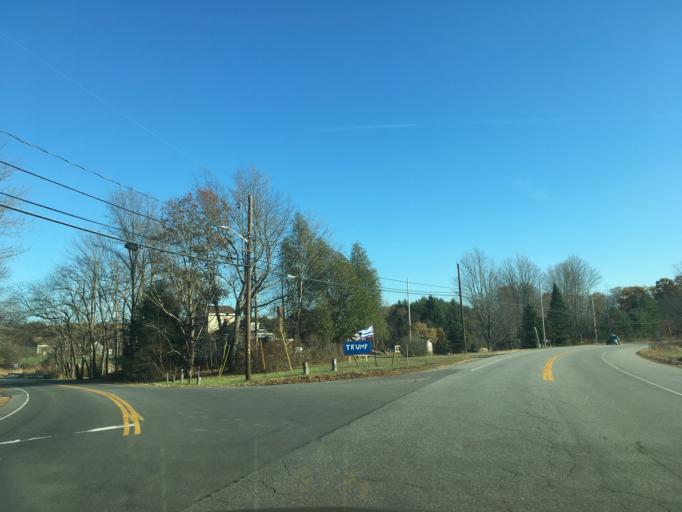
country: US
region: New Hampshire
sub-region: Rockingham County
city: Stratham Station
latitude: 43.0370
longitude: -70.9235
